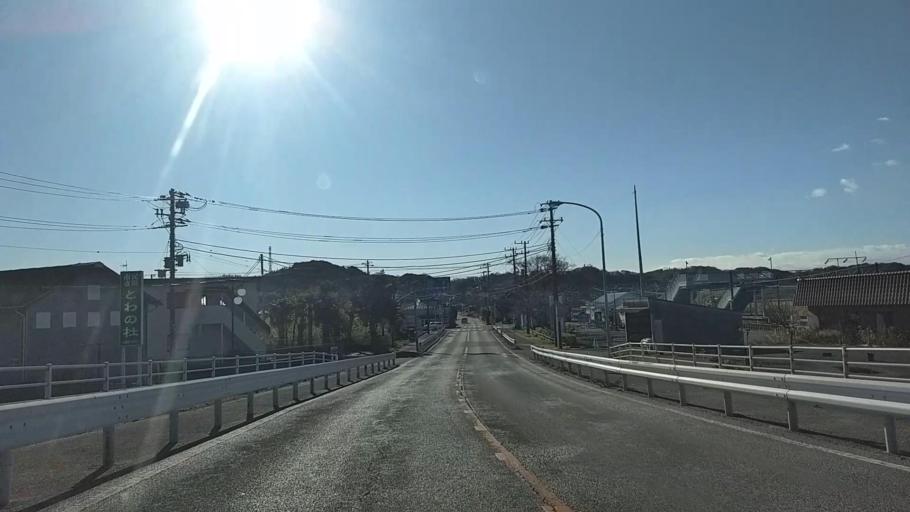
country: JP
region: Chiba
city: Kimitsu
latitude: 35.2619
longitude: 139.8759
